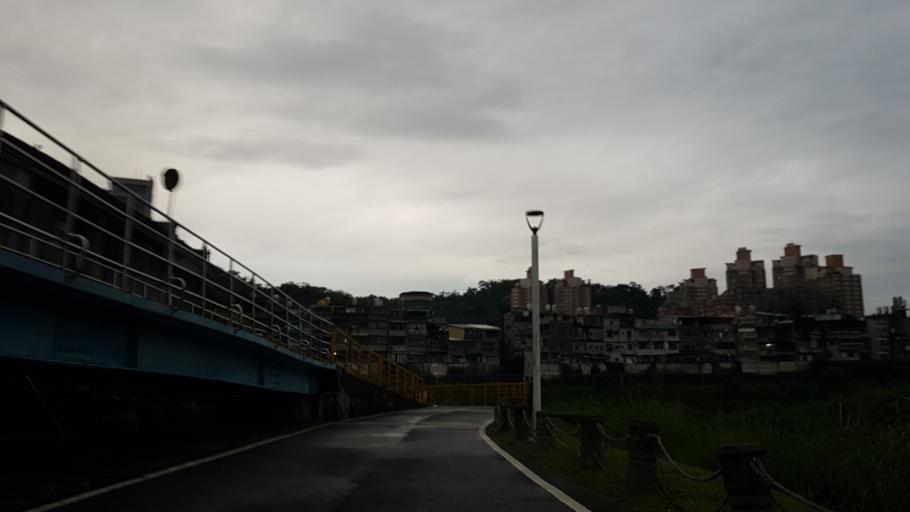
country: TW
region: Taipei
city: Taipei
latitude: 24.9860
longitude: 121.5507
